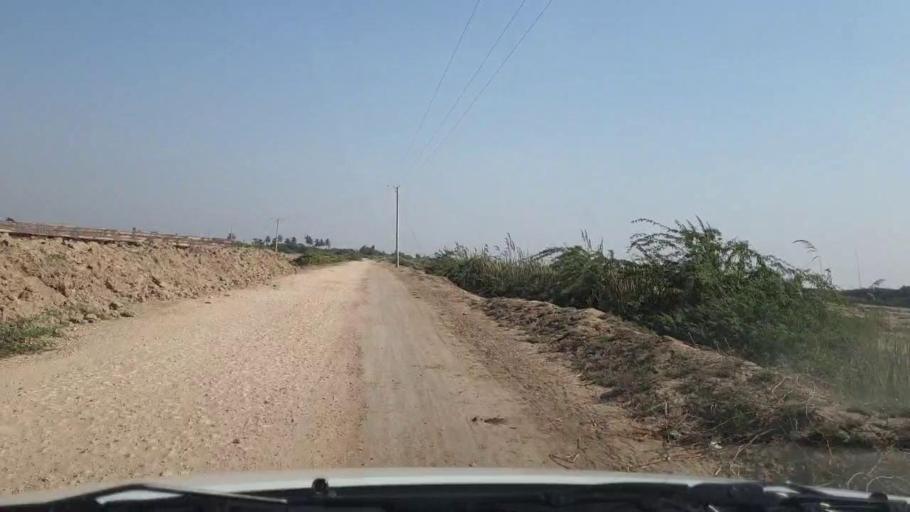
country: PK
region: Sindh
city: Mirpur Sakro
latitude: 24.6483
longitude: 67.6302
